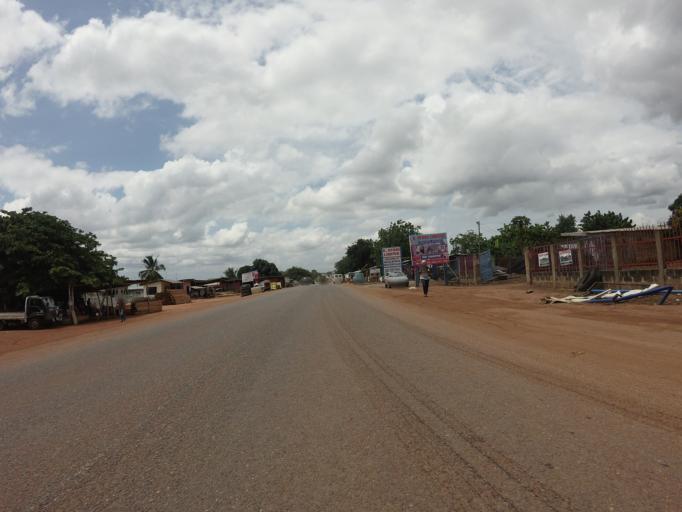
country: GH
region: Eastern
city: Aburi
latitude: 5.8429
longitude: -0.1152
